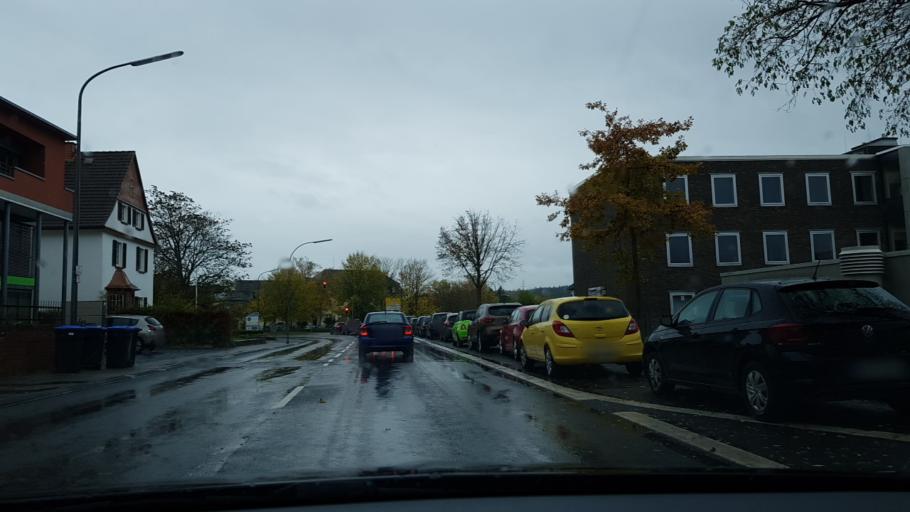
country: DE
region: Rheinland-Pfalz
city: Wittlich
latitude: 49.9836
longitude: 6.8960
